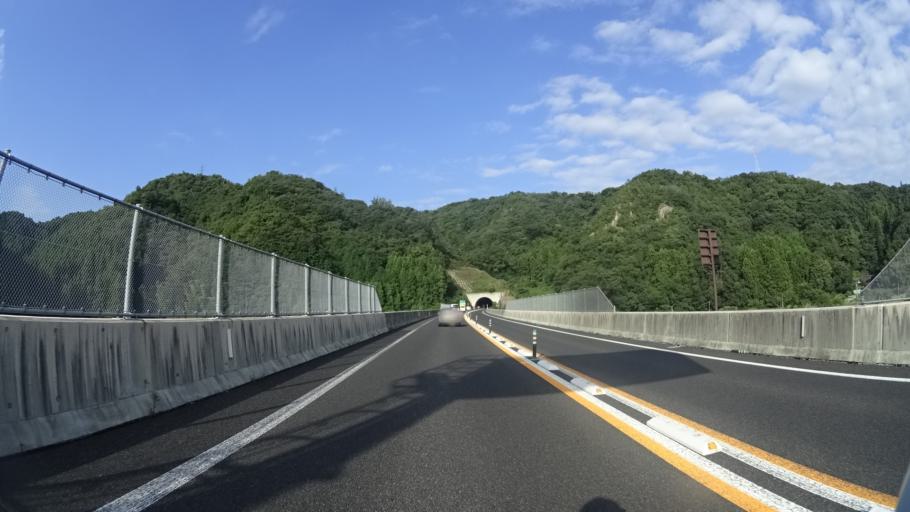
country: JP
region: Shimane
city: Izumo
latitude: 35.3239
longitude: 132.7627
